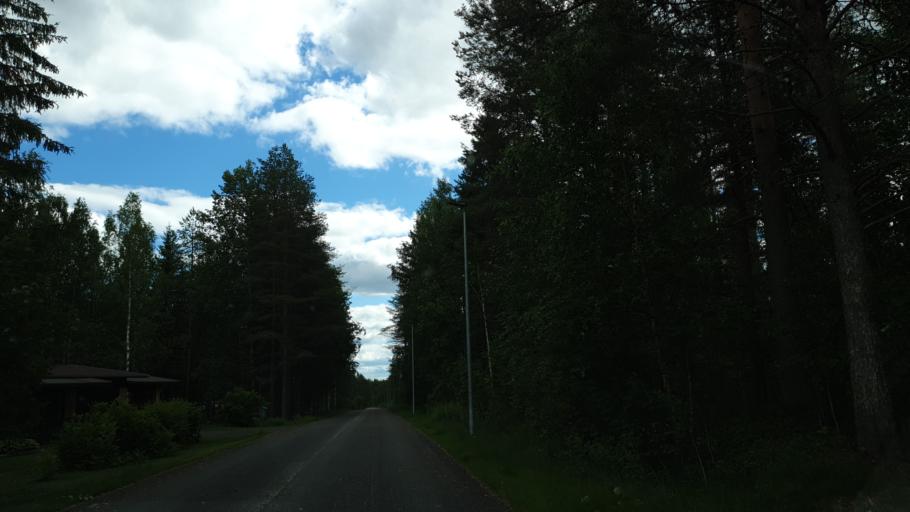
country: FI
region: Kainuu
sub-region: Kehys-Kainuu
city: Kuhmo
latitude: 64.1160
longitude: 29.5082
